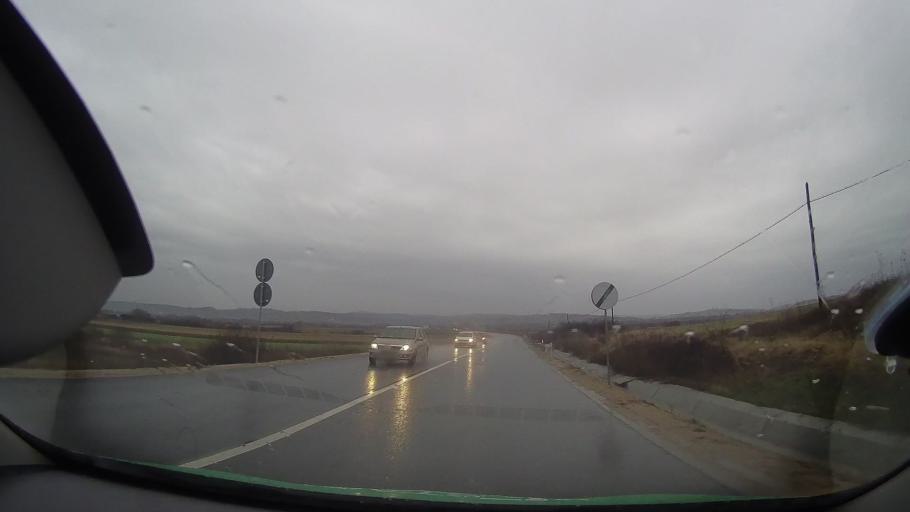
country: RO
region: Bihor
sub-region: Comuna Pocola
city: Pocola
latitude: 46.6851
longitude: 22.3045
